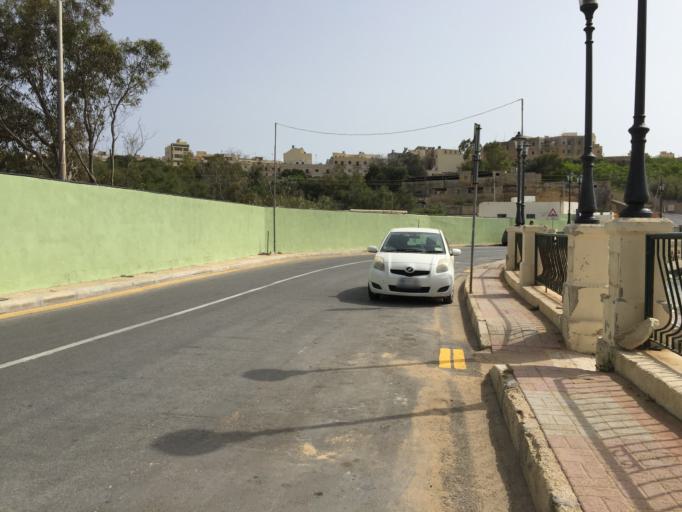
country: MT
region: Il-Kalkara
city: Kalkara
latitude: 35.8934
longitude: 14.5278
